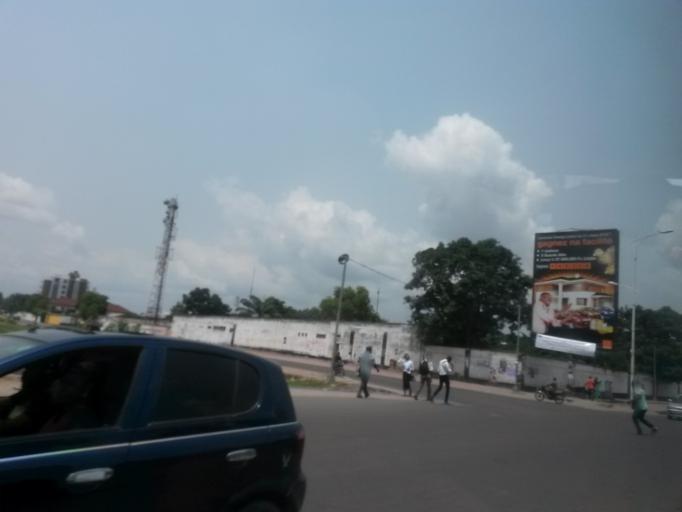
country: CD
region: Kinshasa
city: Kinshasa
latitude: -4.3169
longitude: 15.2924
